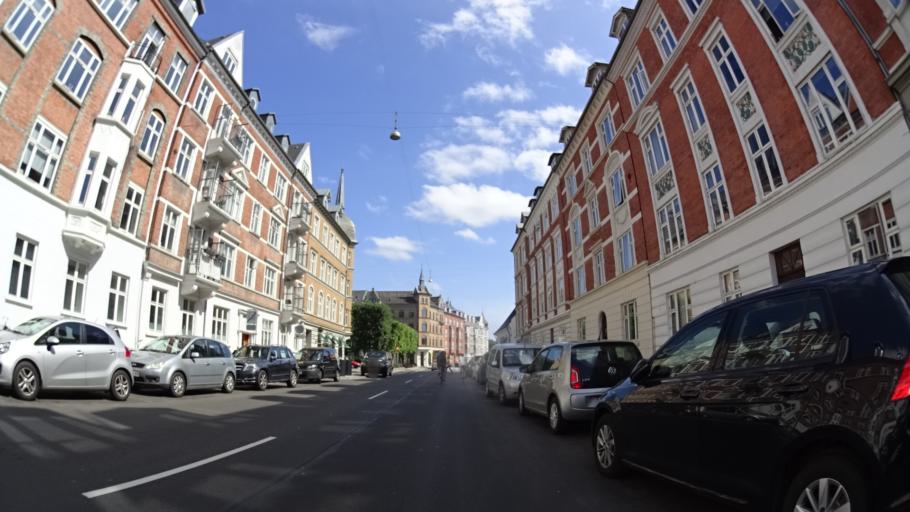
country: DK
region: Central Jutland
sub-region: Arhus Kommune
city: Arhus
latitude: 56.1453
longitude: 10.2029
